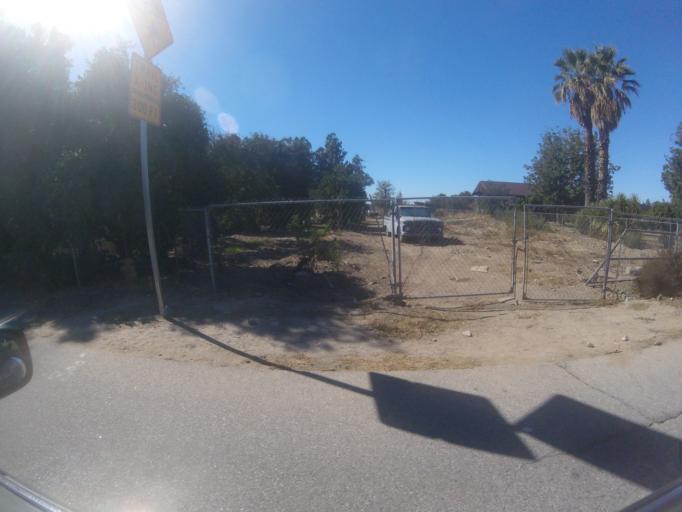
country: US
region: California
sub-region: San Bernardino County
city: Redlands
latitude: 34.0572
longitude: -117.2218
